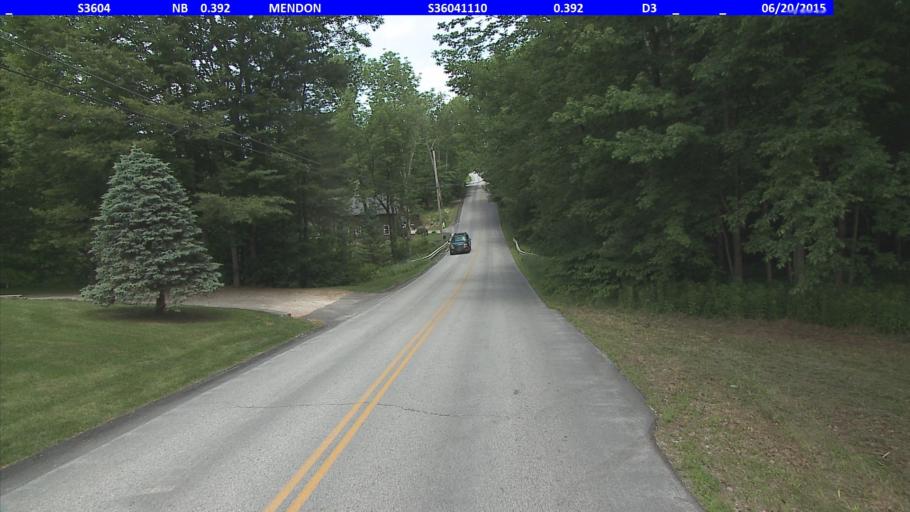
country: US
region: Vermont
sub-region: Rutland County
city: Rutland
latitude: 43.6278
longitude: -72.9369
